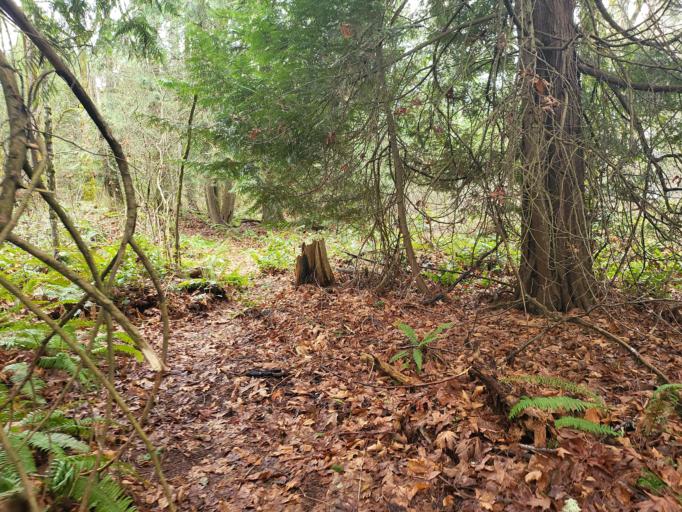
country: US
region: Washington
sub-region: King County
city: Fairwood
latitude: 47.4727
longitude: -122.1541
